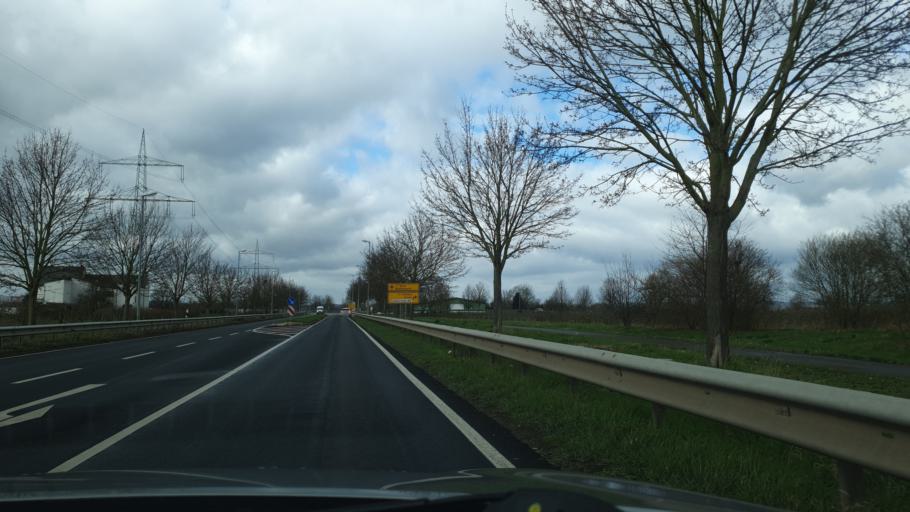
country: DE
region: Rheinland-Pfalz
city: Mulheim-Karlich
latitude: 50.3920
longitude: 7.5083
